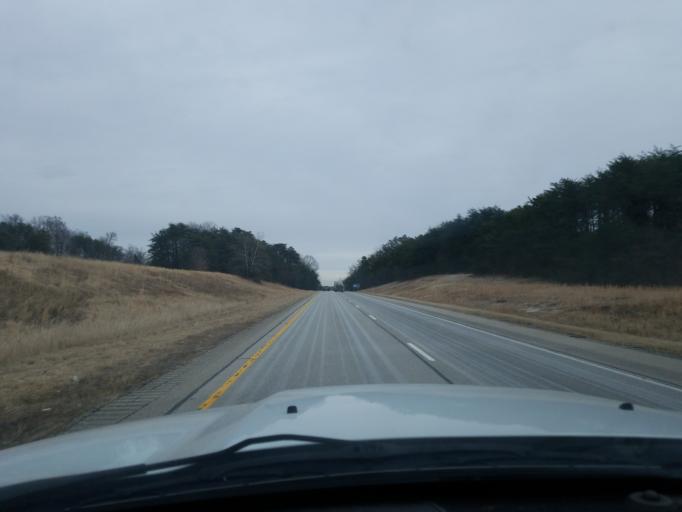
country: US
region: Indiana
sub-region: Floyd County
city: Georgetown
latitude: 38.2771
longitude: -85.9548
